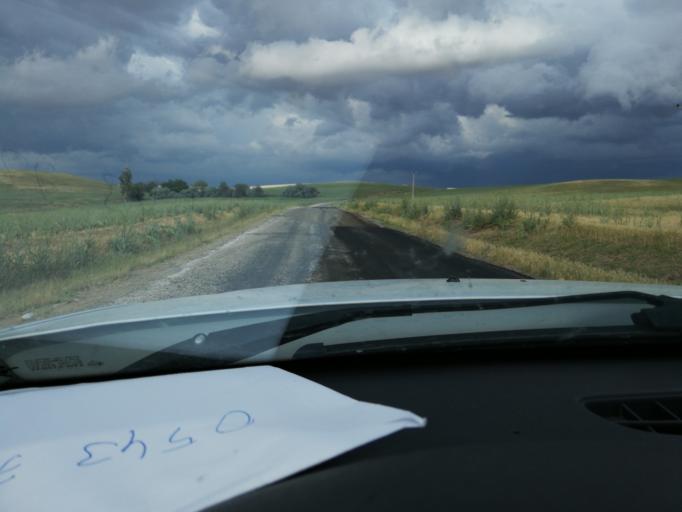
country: TR
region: Kirsehir
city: Kirsehir
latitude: 39.0431
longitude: 34.1611
